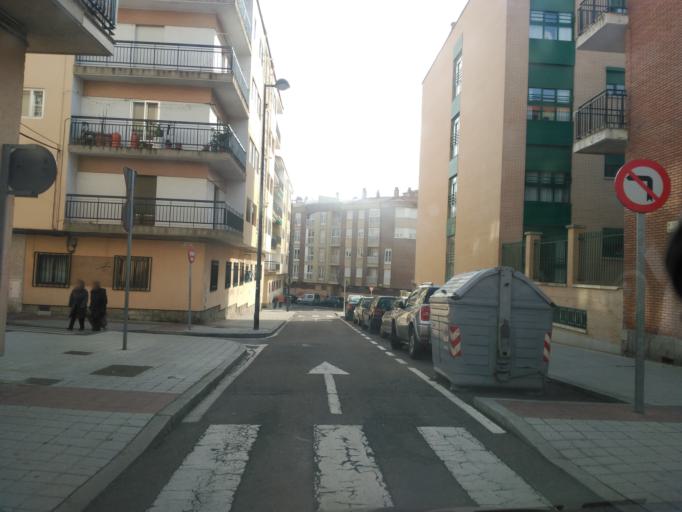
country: ES
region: Castille and Leon
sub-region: Provincia de Salamanca
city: Salamanca
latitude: 40.9648
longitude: -5.6513
